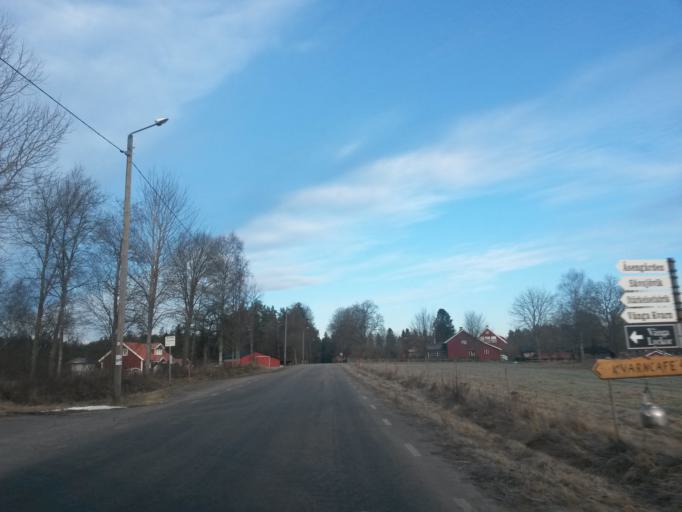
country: SE
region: Vaestra Goetaland
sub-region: Boras Kommun
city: Boras
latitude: 57.8615
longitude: 12.9292
